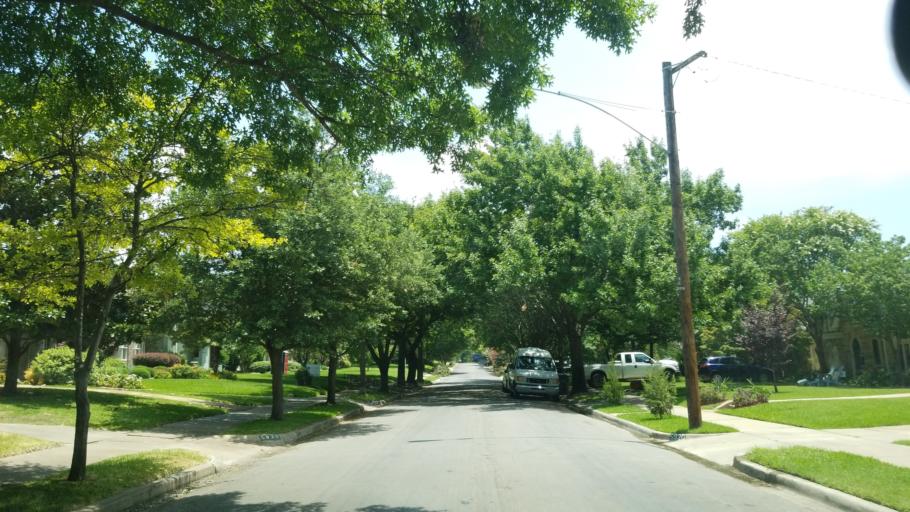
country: US
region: Texas
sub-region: Dallas County
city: Highland Park
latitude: 32.8279
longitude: -96.7647
